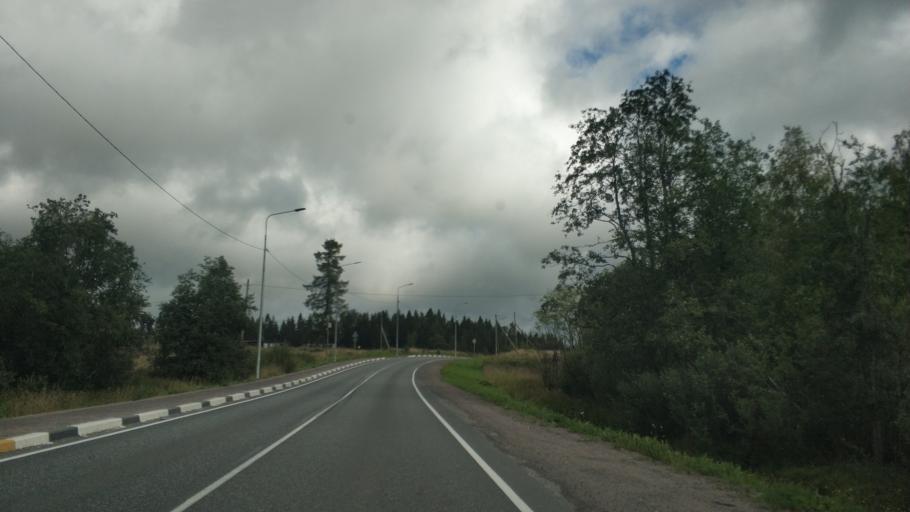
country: RU
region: Republic of Karelia
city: Khelyulya
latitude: 61.7668
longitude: 30.6543
